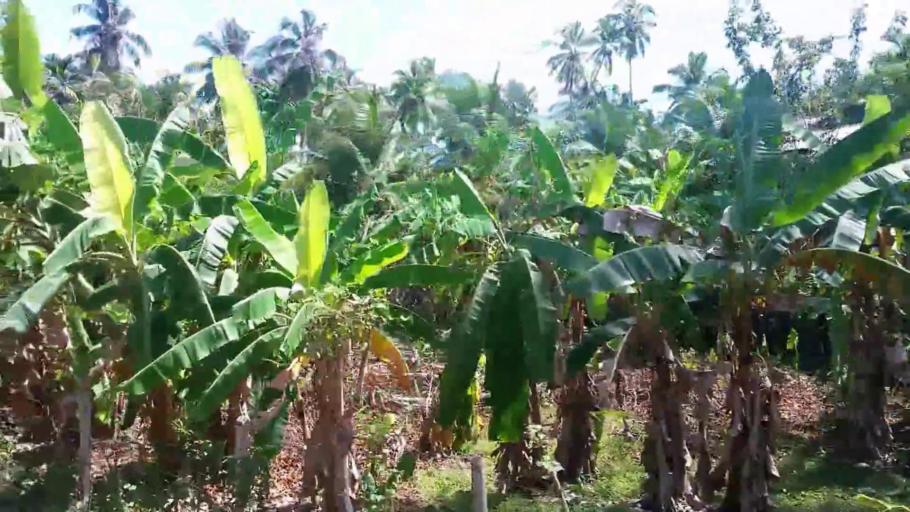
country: LK
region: Southern
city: Hikkaduwa
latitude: 6.1677
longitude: 80.0899
